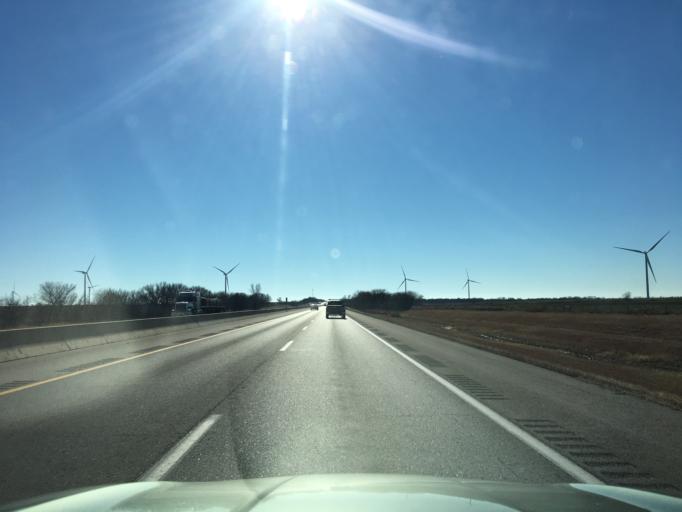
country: US
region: Kansas
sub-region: Sumner County
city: Wellington
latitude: 37.1419
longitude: -97.3394
